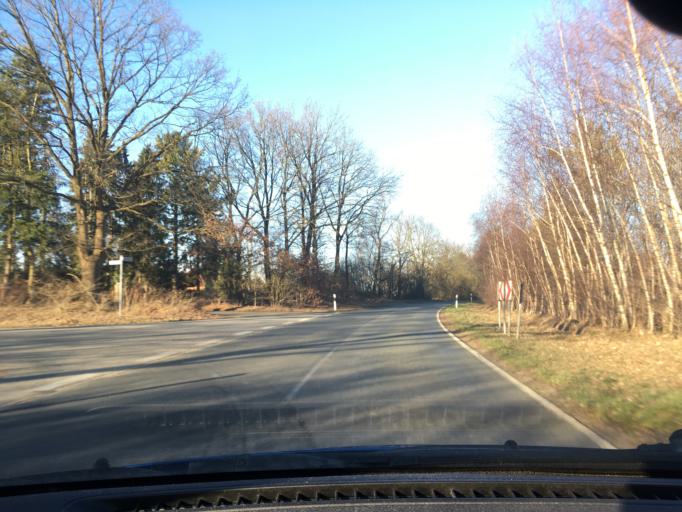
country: DE
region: Schleswig-Holstein
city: Mussen
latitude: 53.4875
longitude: 10.5589
